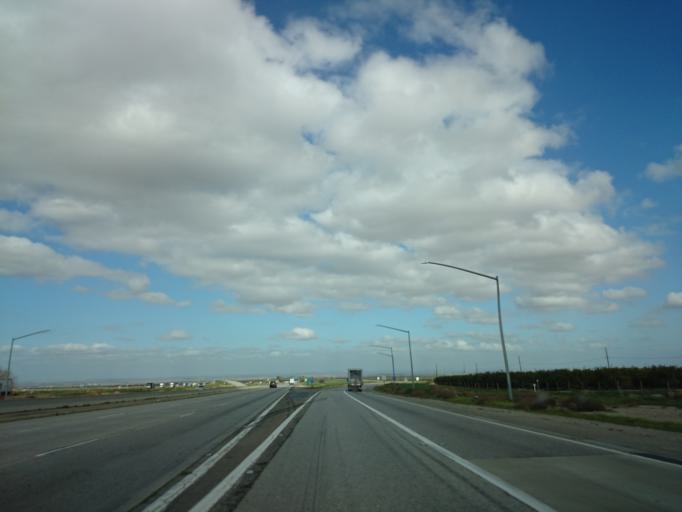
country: US
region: California
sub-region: Kern County
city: Frazier Park
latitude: 35.0069
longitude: -118.9516
